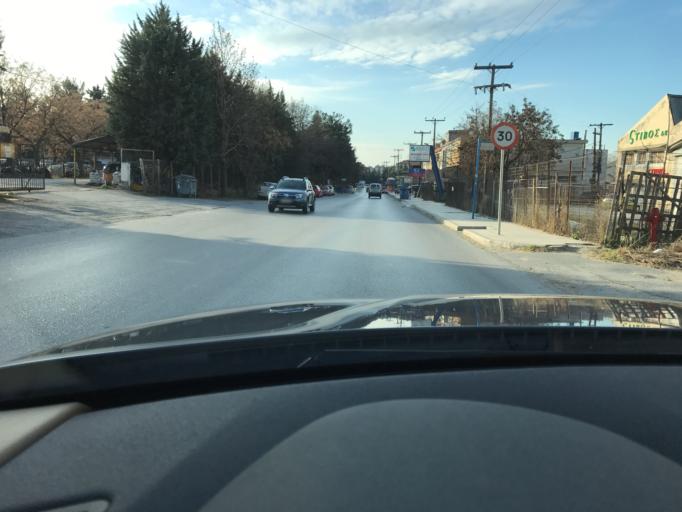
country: GR
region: Central Macedonia
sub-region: Nomos Thessalonikis
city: Efkarpia
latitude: 40.6786
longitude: 22.9463
